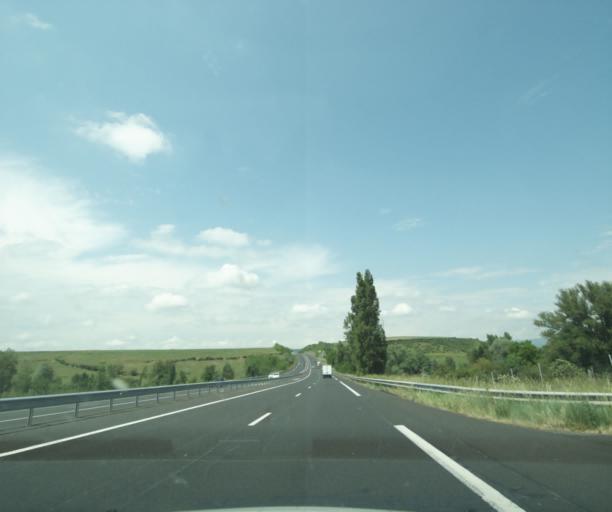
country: FR
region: Auvergne
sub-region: Departement du Puy-de-Dome
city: Le Breuil-sur-Couze
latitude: 45.4505
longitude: 3.2673
